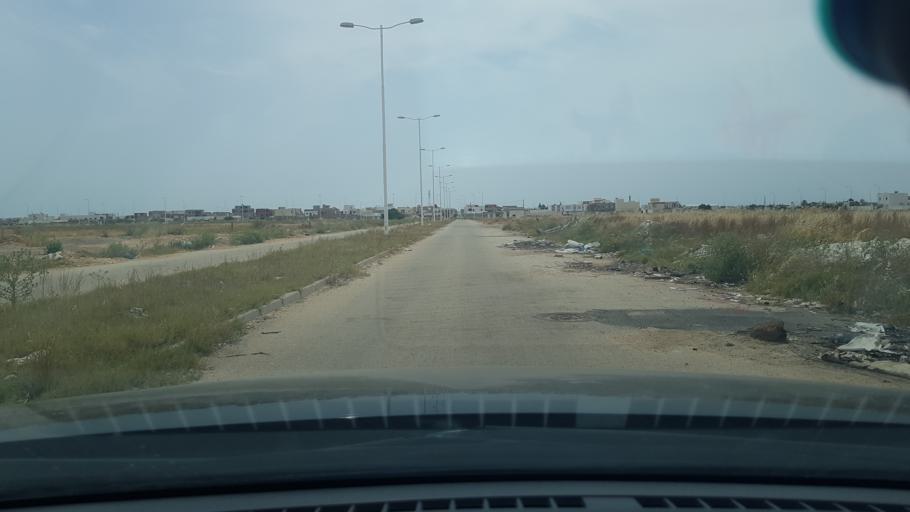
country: TN
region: Safaqis
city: Al Qarmadah
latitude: 34.8296
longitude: 10.7432
